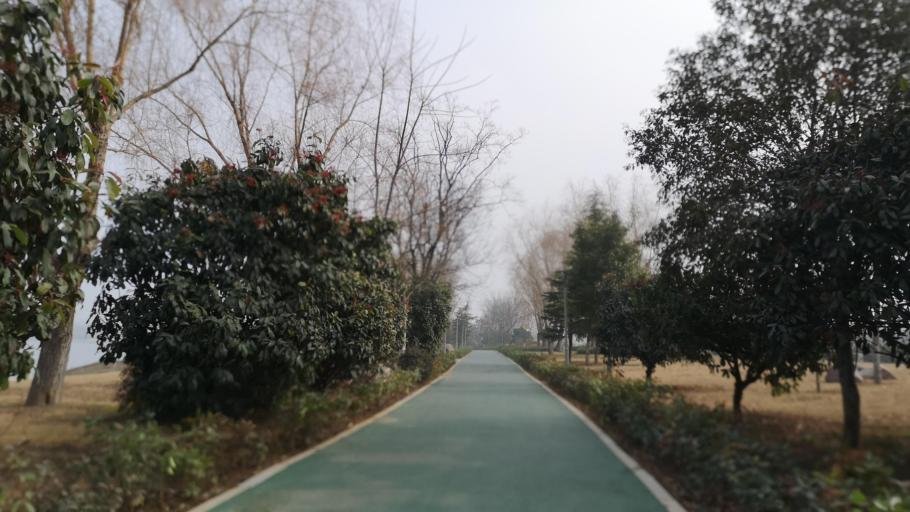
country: CN
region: Henan Sheng
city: Zhongyuanlu
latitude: 35.8002
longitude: 115.0529
